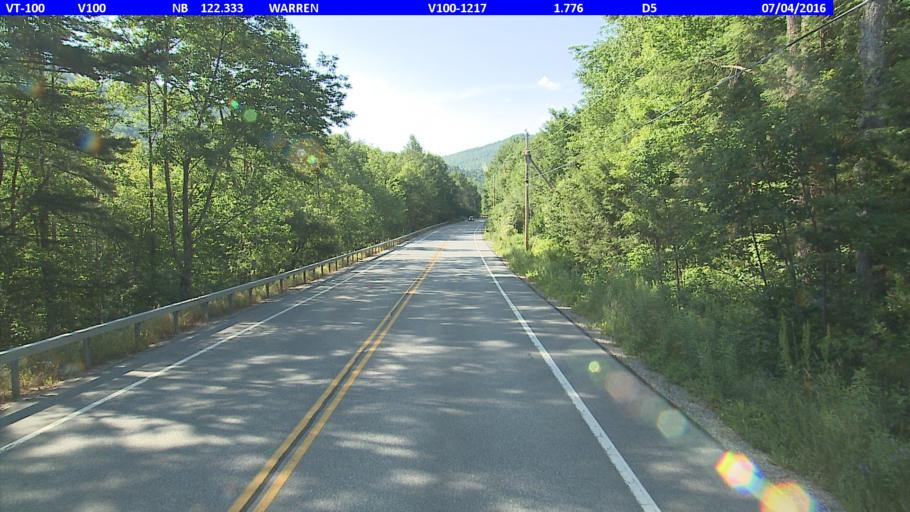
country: US
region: Vermont
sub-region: Washington County
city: Northfield
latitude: 44.0848
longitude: -72.8607
